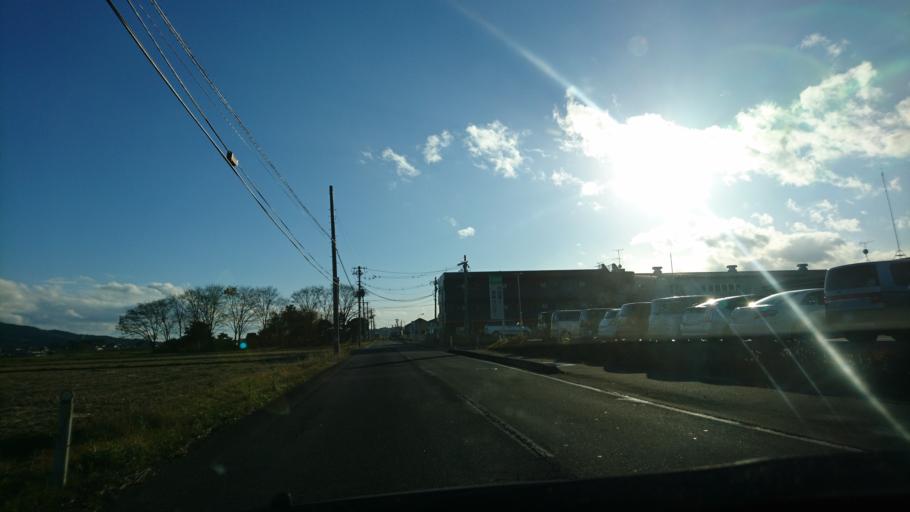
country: JP
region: Iwate
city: Mizusawa
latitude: 39.0517
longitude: 141.1365
